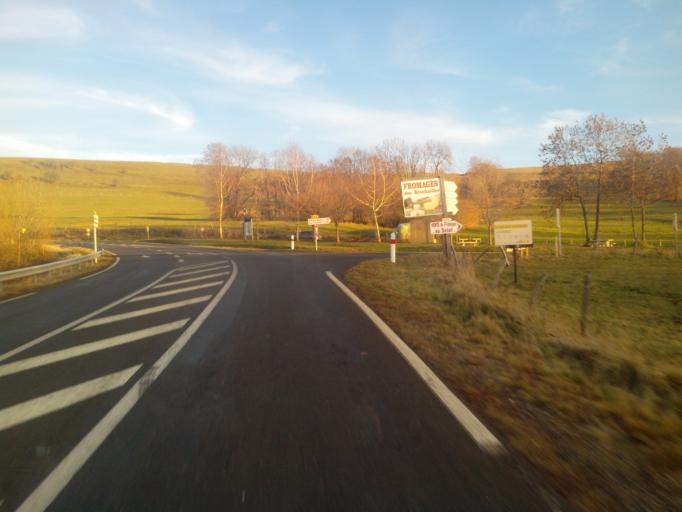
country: FR
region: Auvergne
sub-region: Departement du Cantal
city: Riom-es-Montagnes
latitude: 45.2348
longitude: 2.7335
